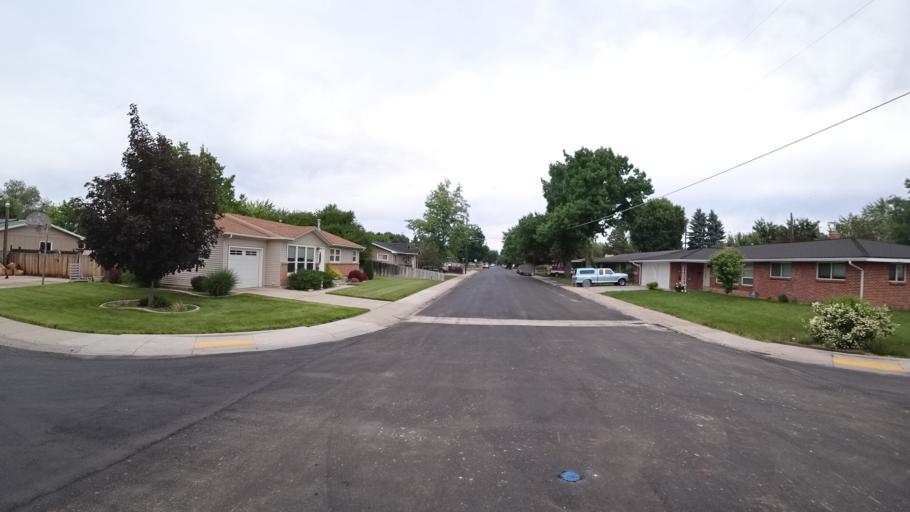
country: US
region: Idaho
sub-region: Ada County
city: Boise
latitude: 43.5762
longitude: -116.2037
